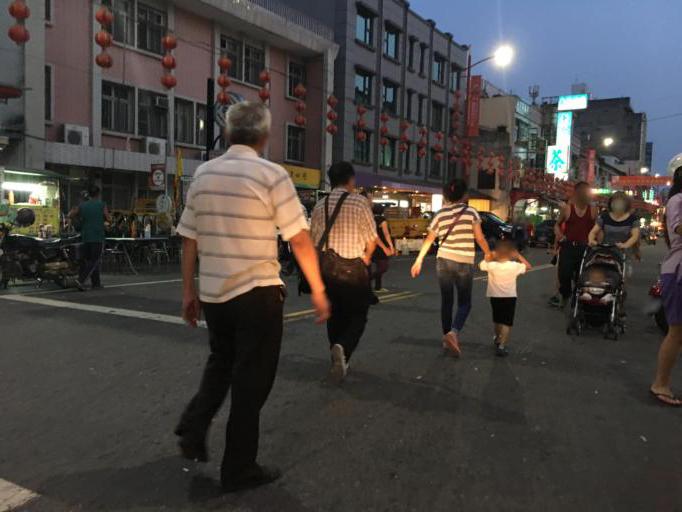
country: TW
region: Taiwan
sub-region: Chiayi
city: Taibao
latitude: 23.5555
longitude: 120.3476
